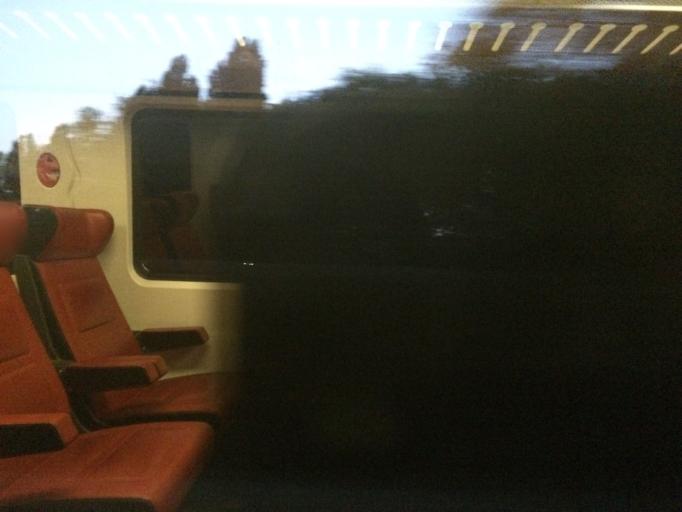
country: NL
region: South Holland
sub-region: Gemeente Dordrecht
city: Dordrecht
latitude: 51.8013
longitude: 4.6784
